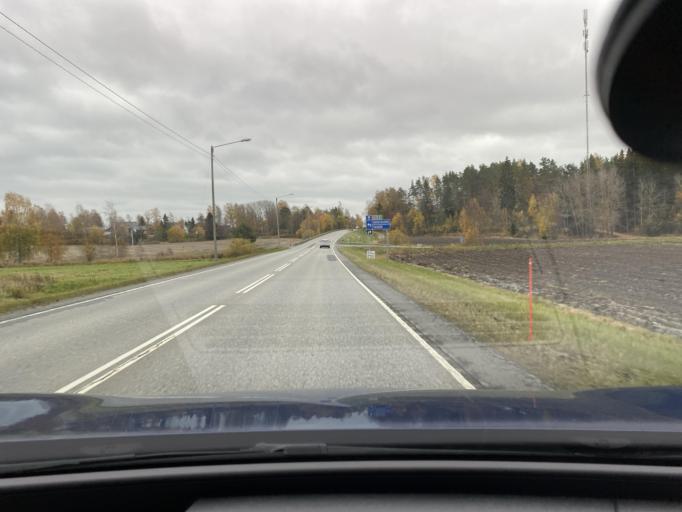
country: FI
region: Varsinais-Suomi
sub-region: Vakka-Suomi
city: Pyhaeranta
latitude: 60.9889
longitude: 21.5841
